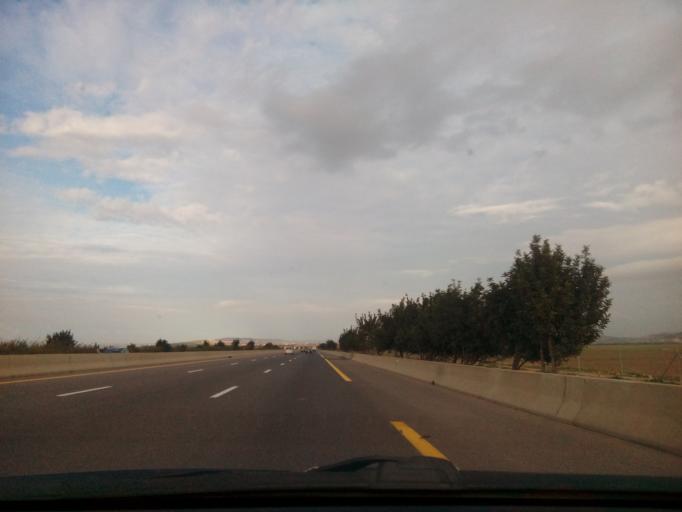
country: DZ
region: Mostaganem
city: Mostaganem
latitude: 35.6727
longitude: 0.1466
